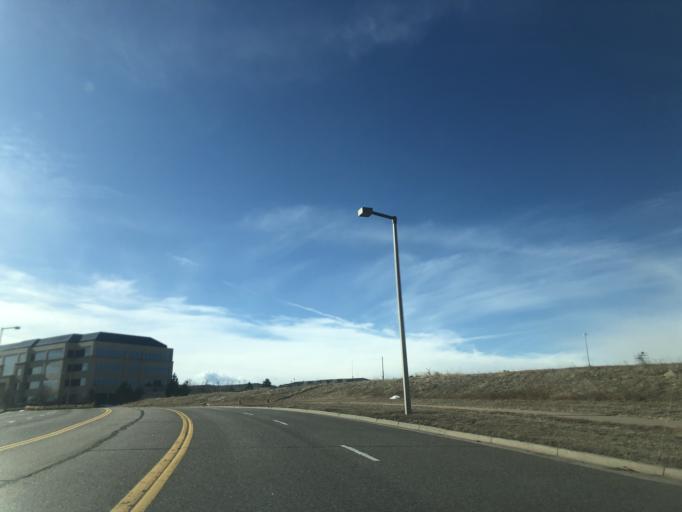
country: US
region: Colorado
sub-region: Douglas County
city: Meridian
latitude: 39.5525
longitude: -104.8651
